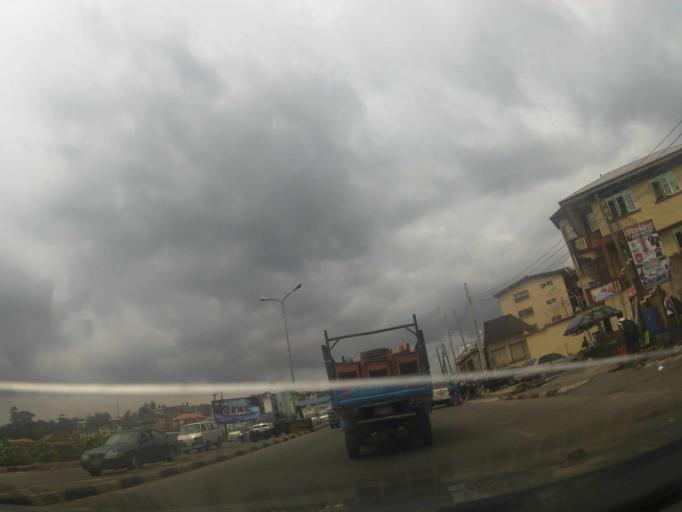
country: NG
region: Oyo
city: Ibadan
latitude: 7.4097
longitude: 3.8907
